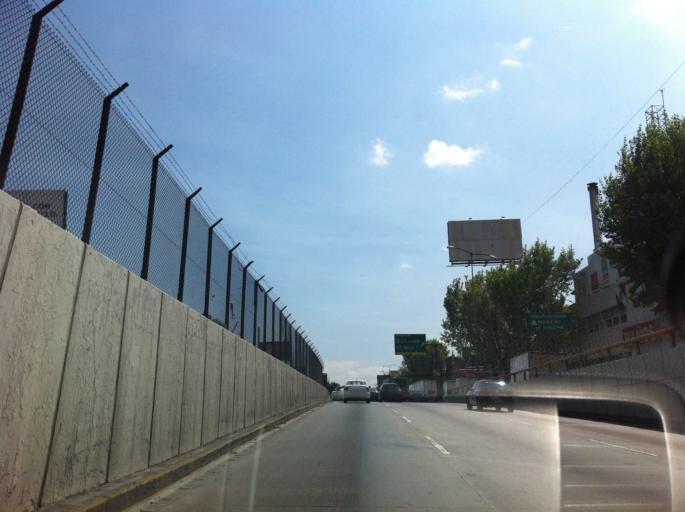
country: MX
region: Mexico City
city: Cuauhtemoc
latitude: 19.4608
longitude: -99.1255
